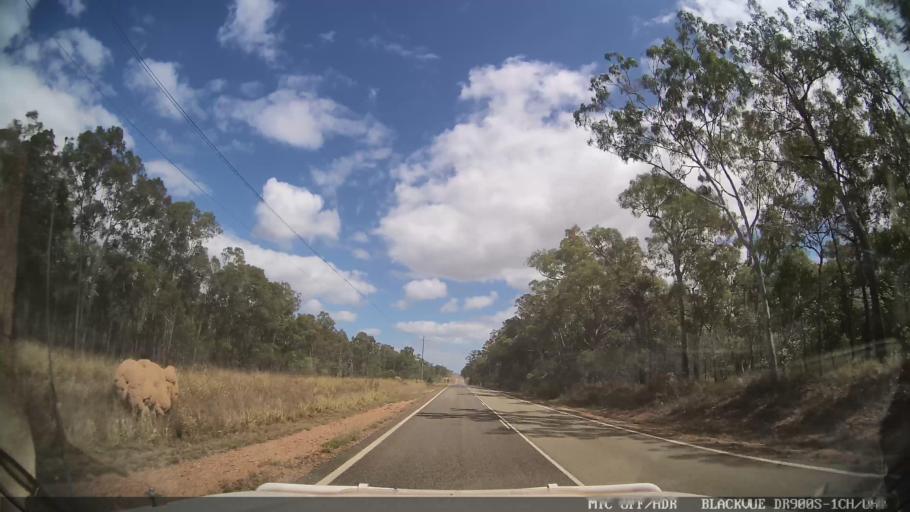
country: AU
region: Queensland
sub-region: Tablelands
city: Ravenshoe
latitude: -17.7218
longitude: 145.0531
